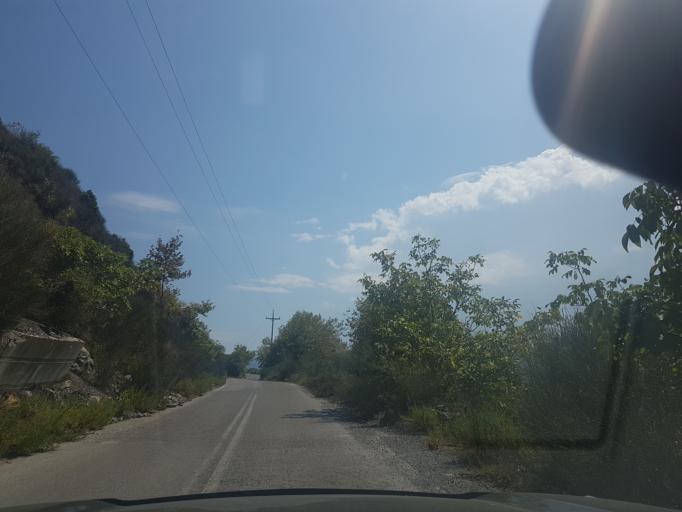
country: GR
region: Central Greece
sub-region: Nomos Evvoias
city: Yimnon
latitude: 38.6399
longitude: 23.8937
